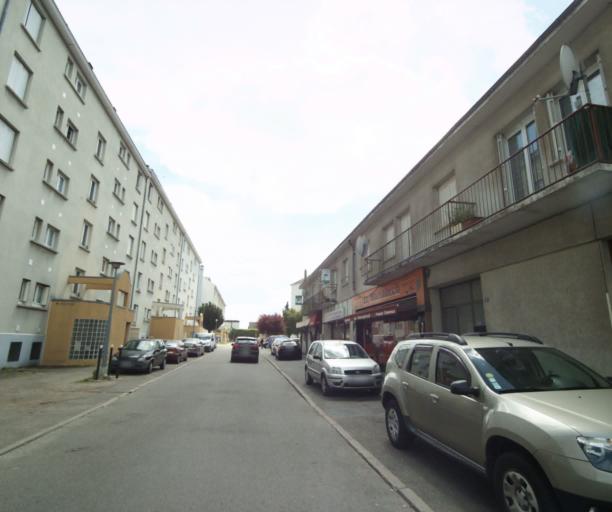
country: FR
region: Centre
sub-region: Departement d'Eure-et-Loir
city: Luce
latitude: 48.4392
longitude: 1.4612
